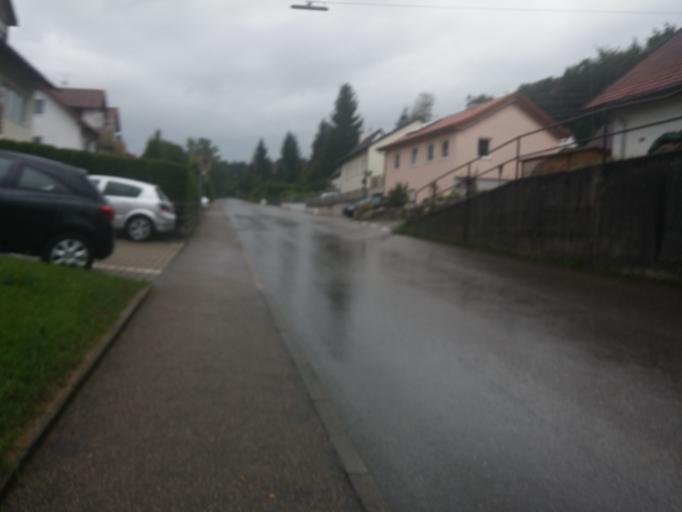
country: DE
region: Bavaria
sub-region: Swabia
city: Woringen
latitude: 47.8725
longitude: 10.2200
